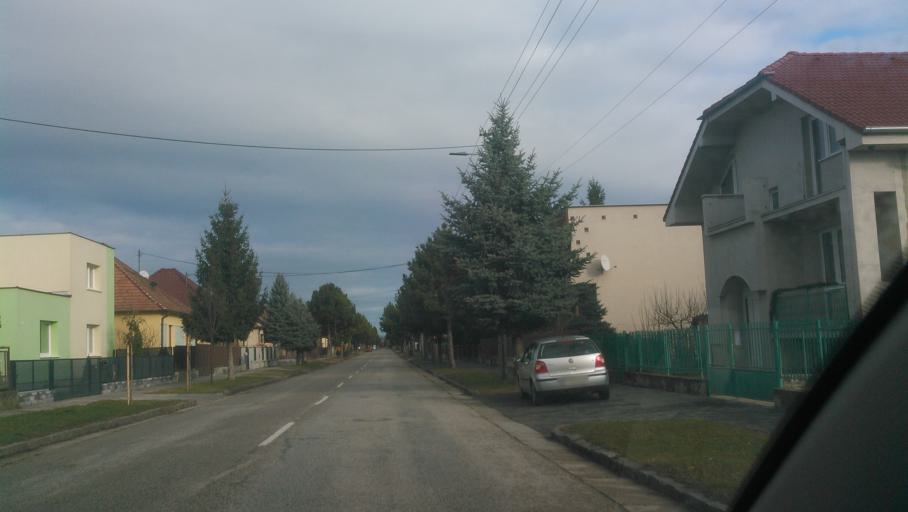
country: SK
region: Trnavsky
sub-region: Okres Trnava
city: Trnava
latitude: 48.3165
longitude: 17.6489
